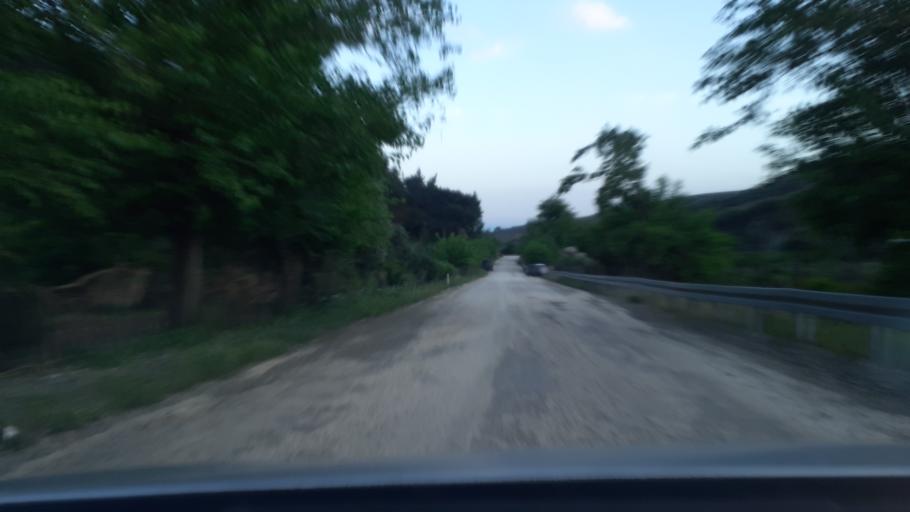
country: TR
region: Hatay
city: Kirikhan
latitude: 36.5214
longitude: 36.3182
